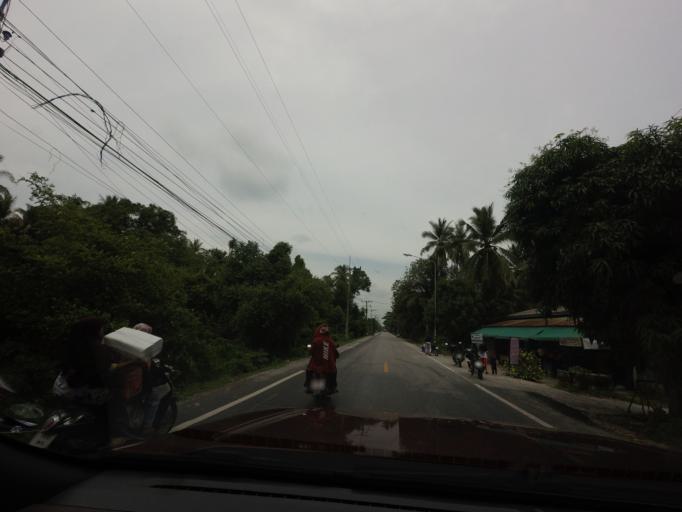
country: TH
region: Pattani
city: Yaring
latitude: 6.8552
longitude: 101.3611
